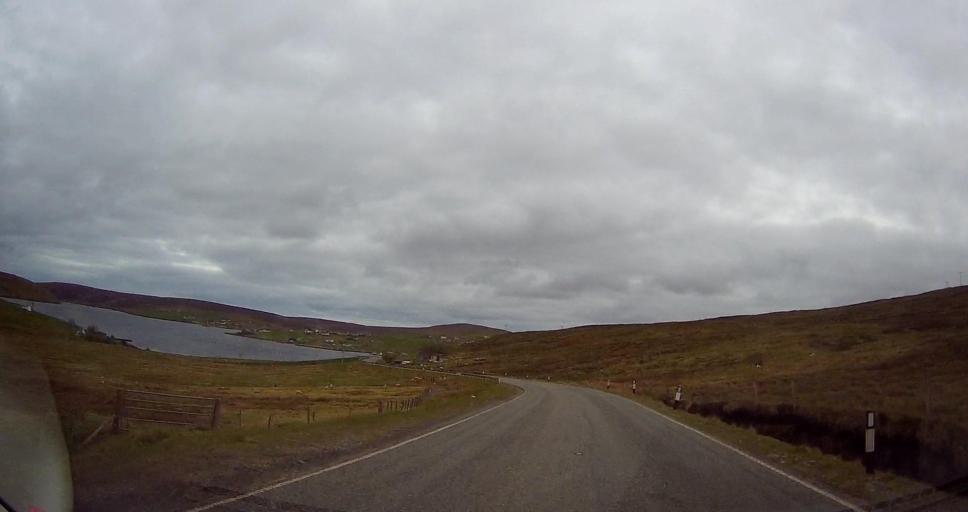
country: GB
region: Scotland
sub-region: Shetland Islands
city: Shetland
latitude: 60.6153
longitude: -1.0745
